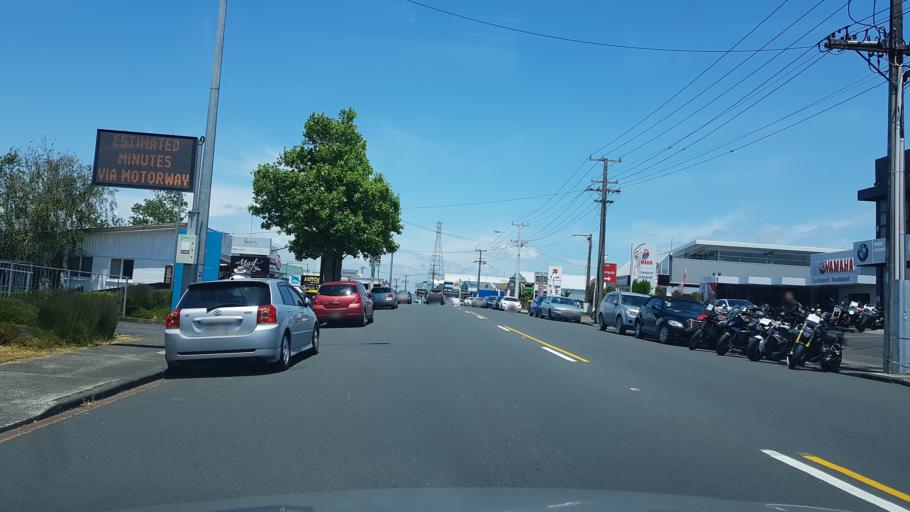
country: NZ
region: Auckland
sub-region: Auckland
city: North Shore
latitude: -36.7937
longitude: 174.7652
